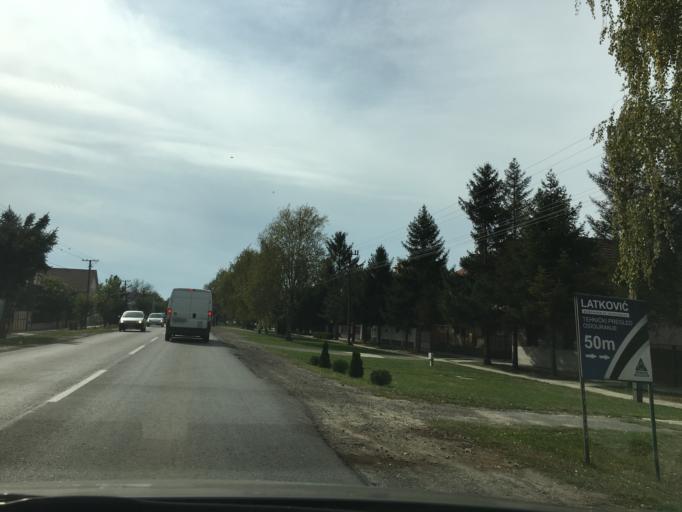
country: RS
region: Autonomna Pokrajina Vojvodina
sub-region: Juznobacki Okrug
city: Temerin
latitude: 45.3857
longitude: 19.8788
